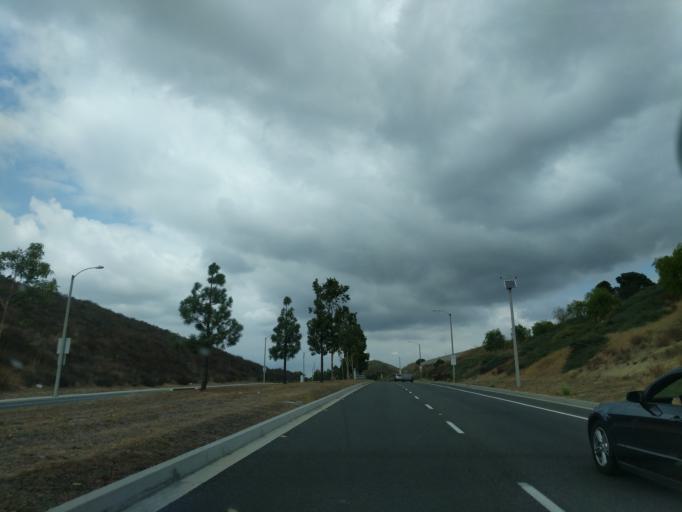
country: US
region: California
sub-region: Orange County
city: North Tustin
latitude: 33.7725
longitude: -117.7596
